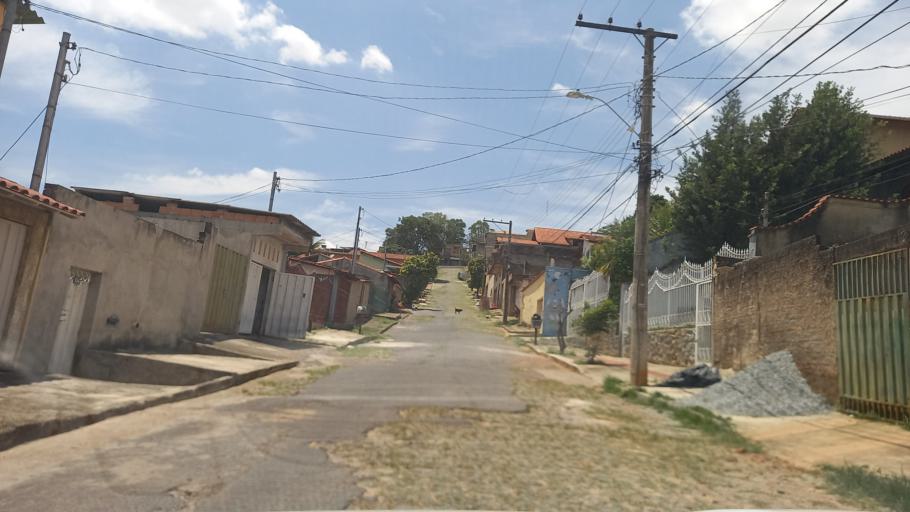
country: BR
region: Minas Gerais
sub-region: Contagem
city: Contagem
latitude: -19.9059
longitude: -44.0116
